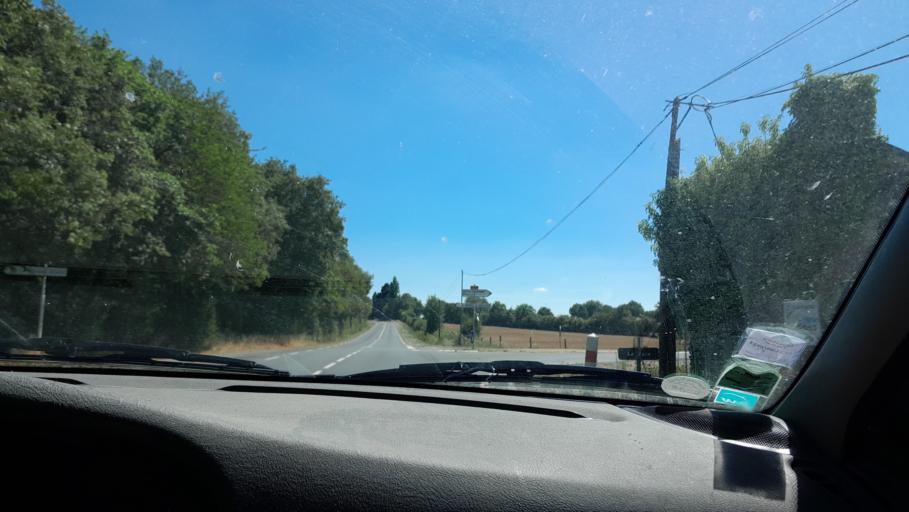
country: FR
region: Pays de la Loire
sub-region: Departement de la Loire-Atlantique
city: Saint-Mars-la-Jaille
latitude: 47.6054
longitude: -1.2017
